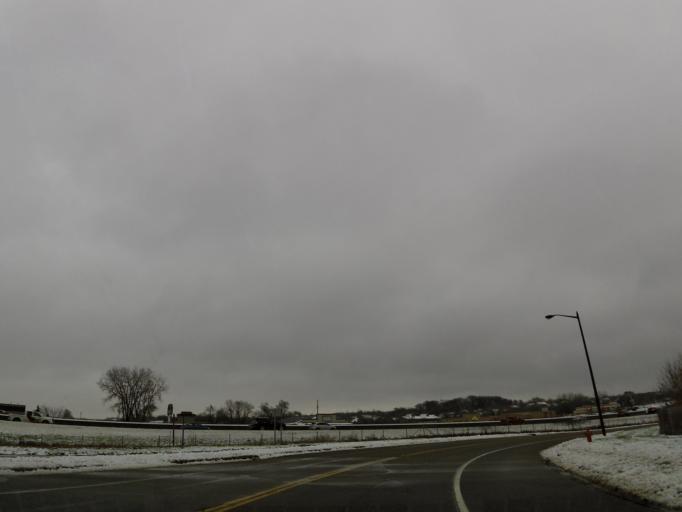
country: US
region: Minnesota
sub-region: Dakota County
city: Burnsville
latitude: 44.7137
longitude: -93.2848
